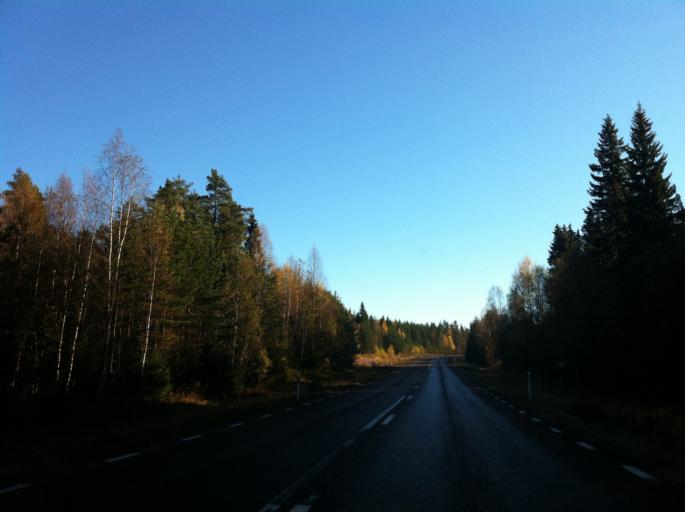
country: SE
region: Dalarna
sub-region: Alvdalens Kommun
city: AElvdalen
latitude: 61.1708
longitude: 14.1054
